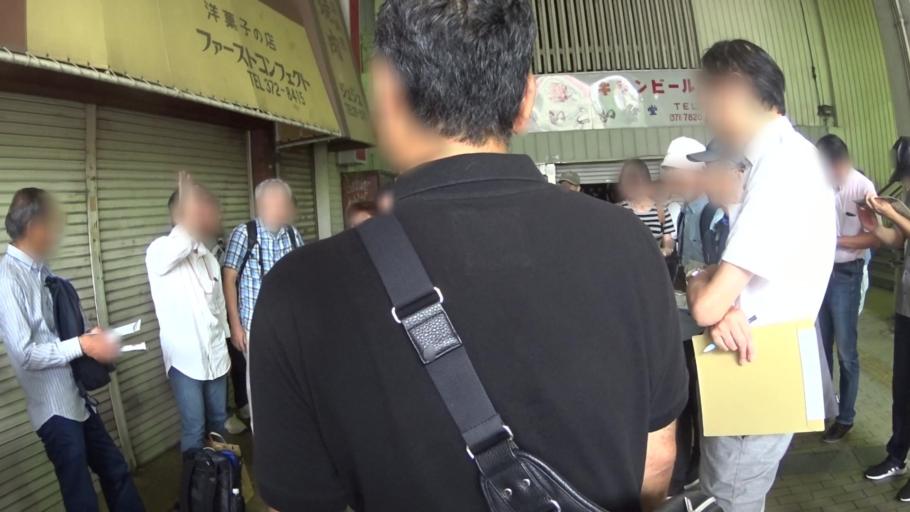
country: JP
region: Osaka
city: Osaka-shi
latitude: 34.7093
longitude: 135.4908
